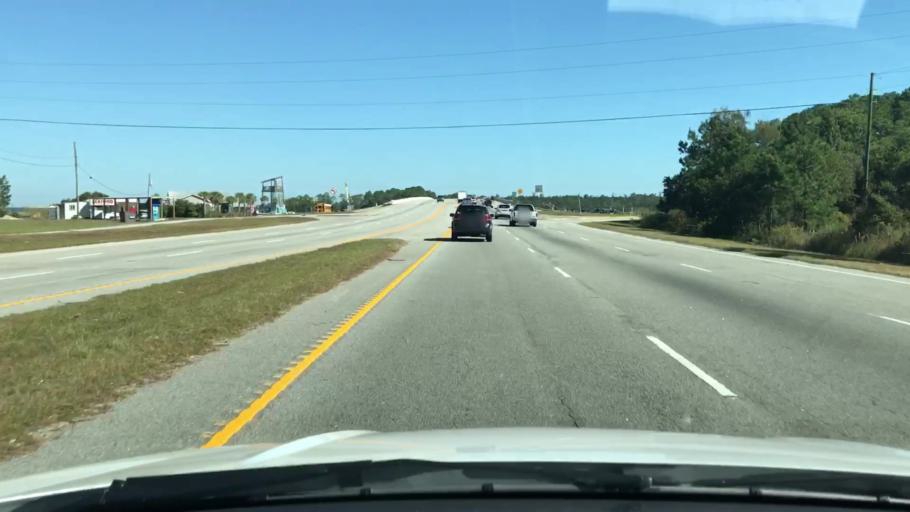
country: US
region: South Carolina
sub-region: Beaufort County
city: Laurel Bay
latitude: 32.3738
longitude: -80.8401
